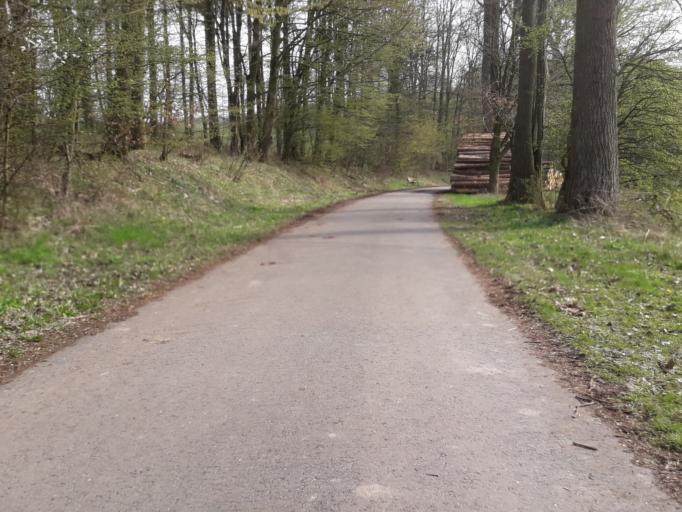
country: DE
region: North Rhine-Westphalia
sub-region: Regierungsbezirk Detmold
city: Paderborn
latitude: 51.6747
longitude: 8.7852
